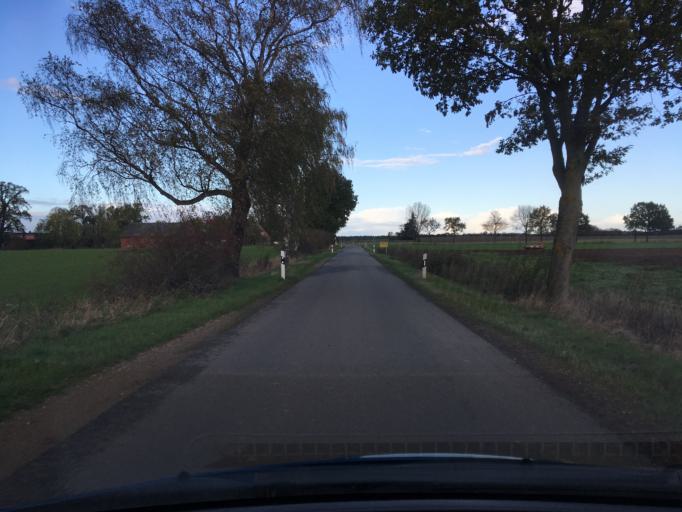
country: DE
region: Lower Saxony
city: Reinstorf
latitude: 53.2628
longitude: 10.5655
